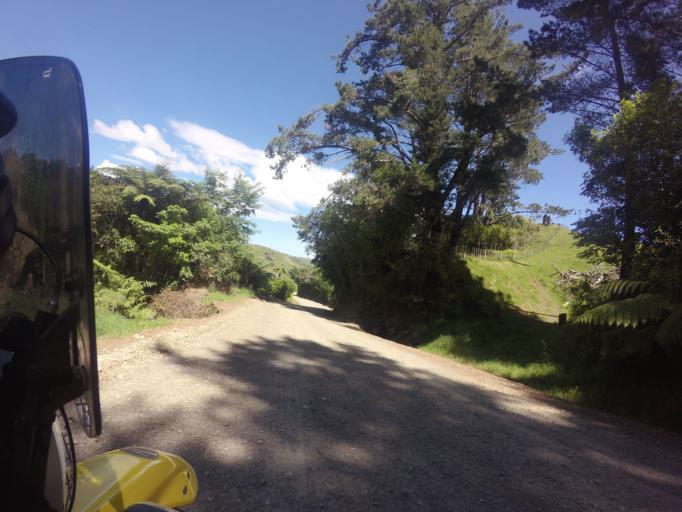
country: NZ
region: Hawke's Bay
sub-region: Wairoa District
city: Wairoa
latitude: -38.9777
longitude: 177.7034
